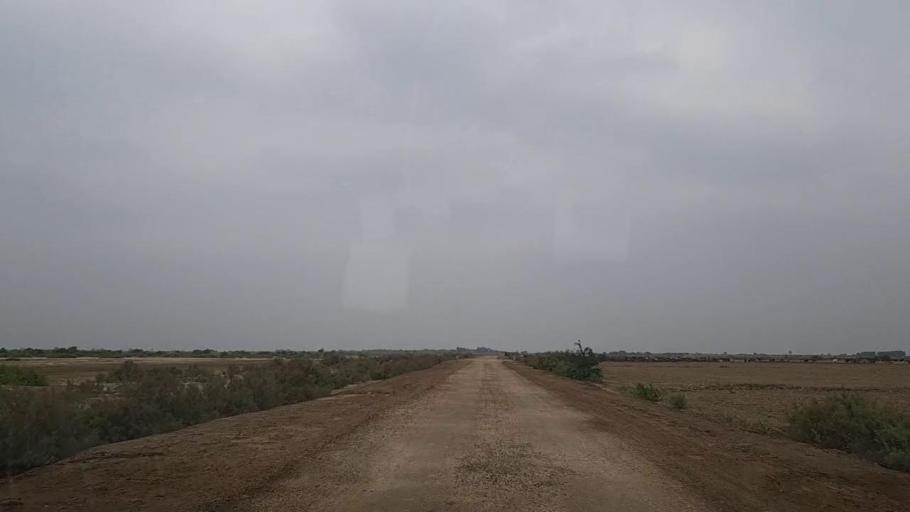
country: PK
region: Sindh
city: Mirpur Sakro
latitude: 24.6273
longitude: 67.7189
